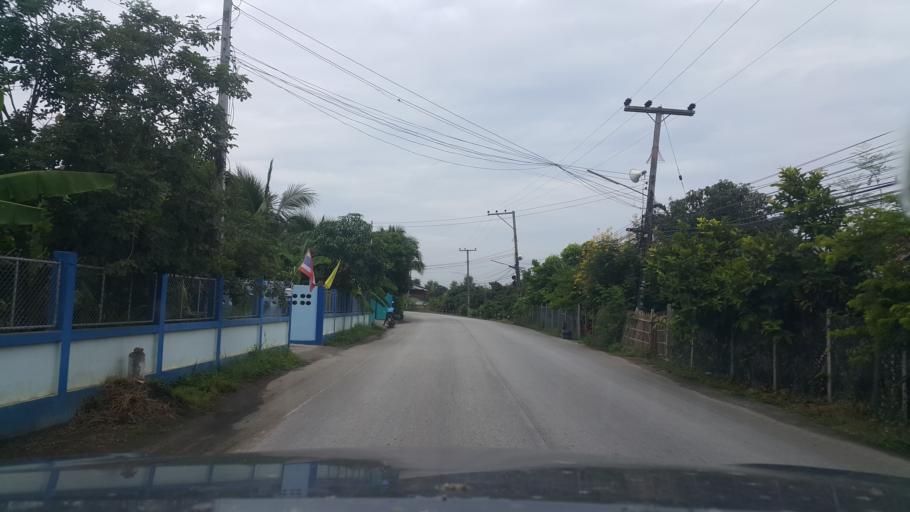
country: TH
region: Chiang Mai
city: San Pa Tong
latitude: 18.6478
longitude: 98.8395
